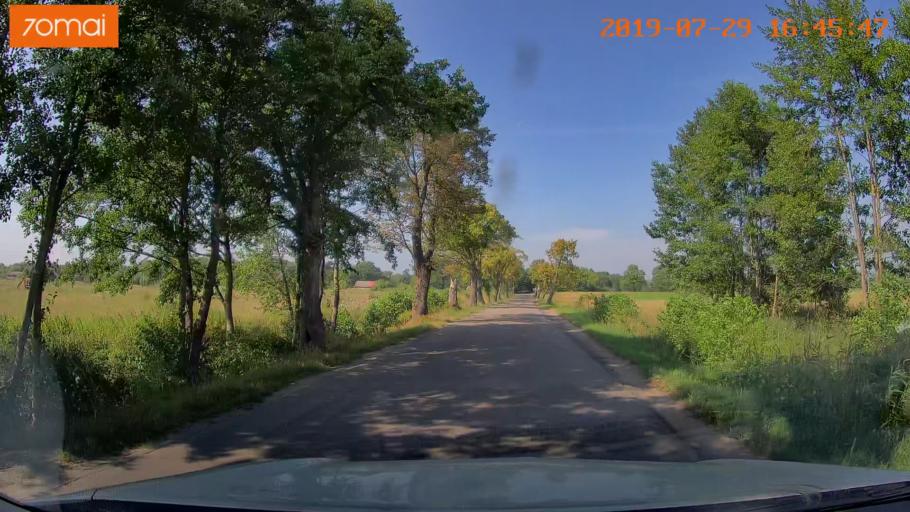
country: RU
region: Kaliningrad
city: Primorsk
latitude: 54.7680
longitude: 20.0797
